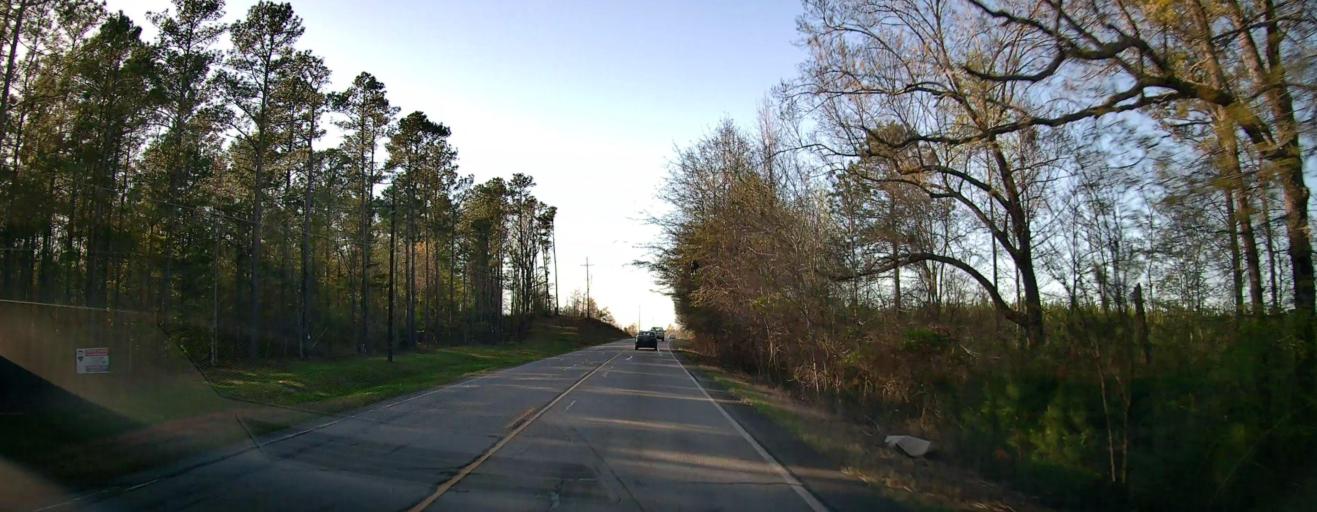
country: US
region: Georgia
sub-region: Butts County
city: Jackson
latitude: 33.4114
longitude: -83.8917
